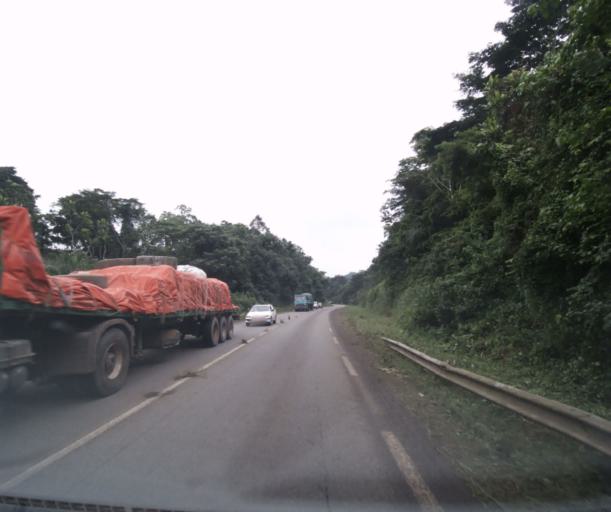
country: CM
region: Littoral
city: Edea
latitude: 3.8235
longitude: 10.3835
